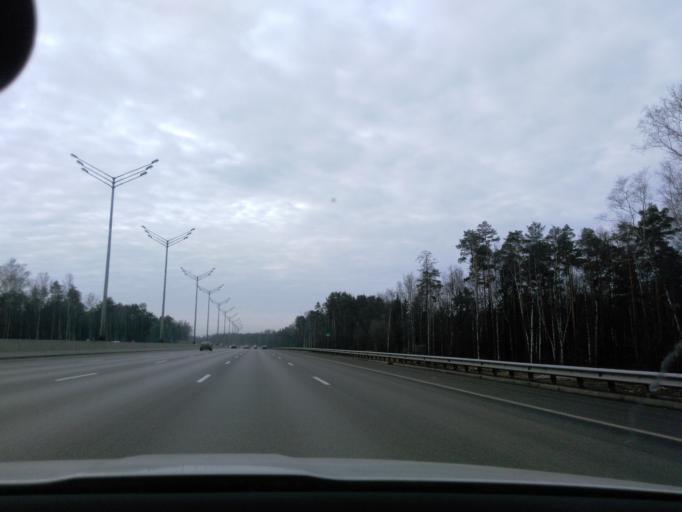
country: RU
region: Moscow
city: Khimki
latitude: 55.9261
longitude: 37.4538
